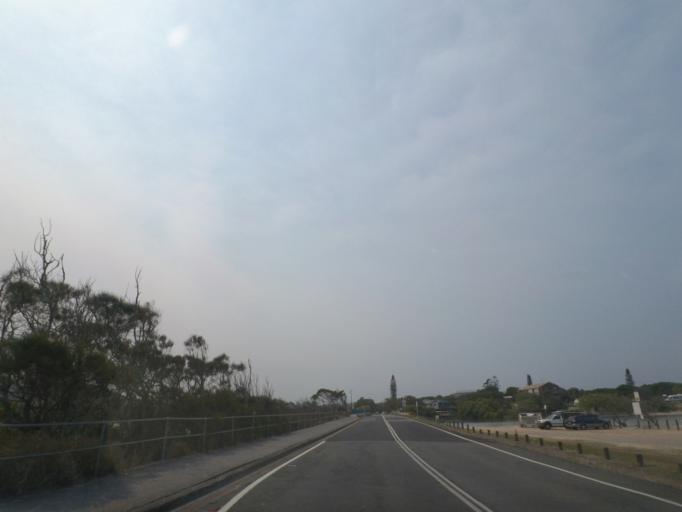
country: AU
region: New South Wales
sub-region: Tweed
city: Pottsville Beach
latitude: -28.3597
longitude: 153.5742
